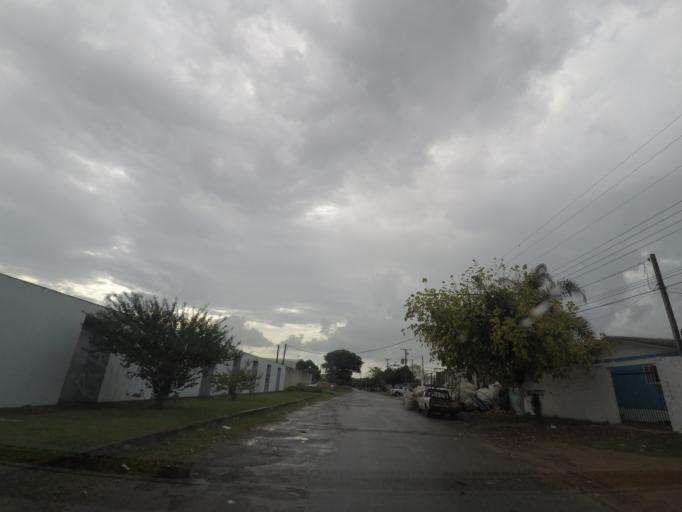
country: BR
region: Parana
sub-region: Sao Jose Dos Pinhais
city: Sao Jose dos Pinhais
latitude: -25.4817
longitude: -49.2389
